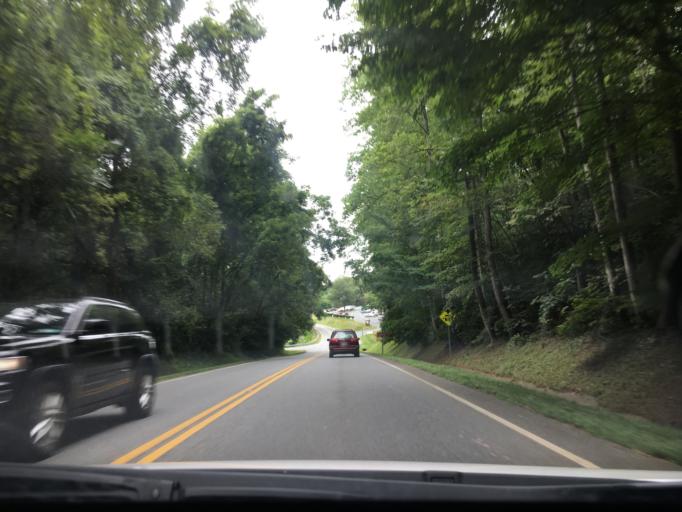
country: US
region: Virginia
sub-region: City of Charlottesville
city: Charlottesville
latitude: 38.0079
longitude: -78.4674
